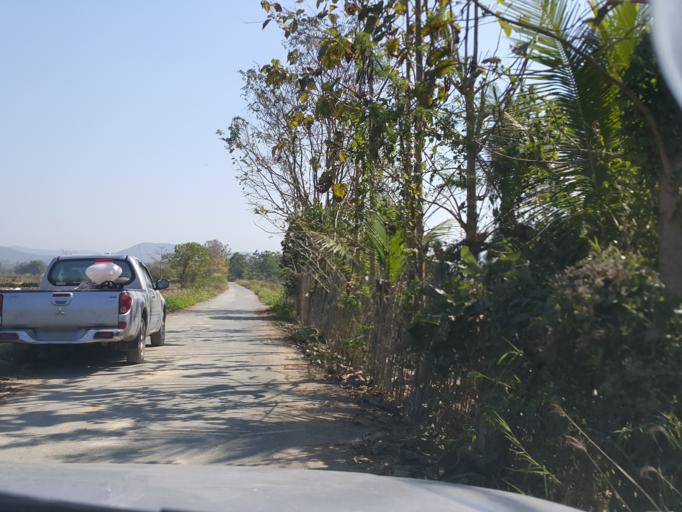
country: TH
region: Chiang Mai
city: San Sai
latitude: 18.8368
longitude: 99.1342
